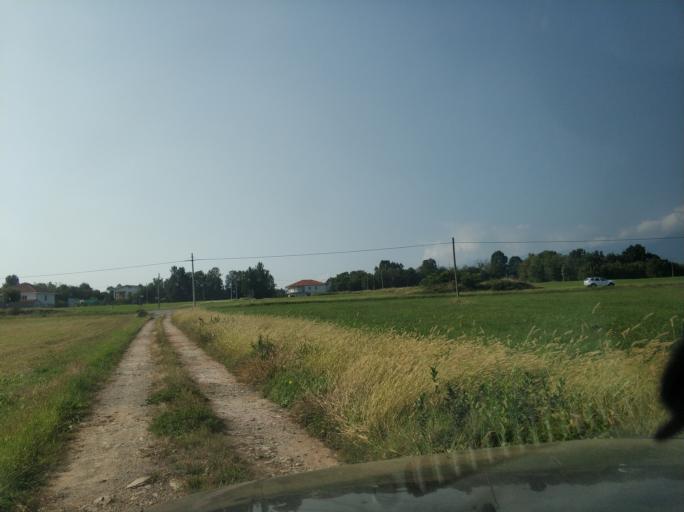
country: IT
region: Piedmont
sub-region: Provincia di Torino
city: Nole
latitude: 45.2559
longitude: 7.5866
